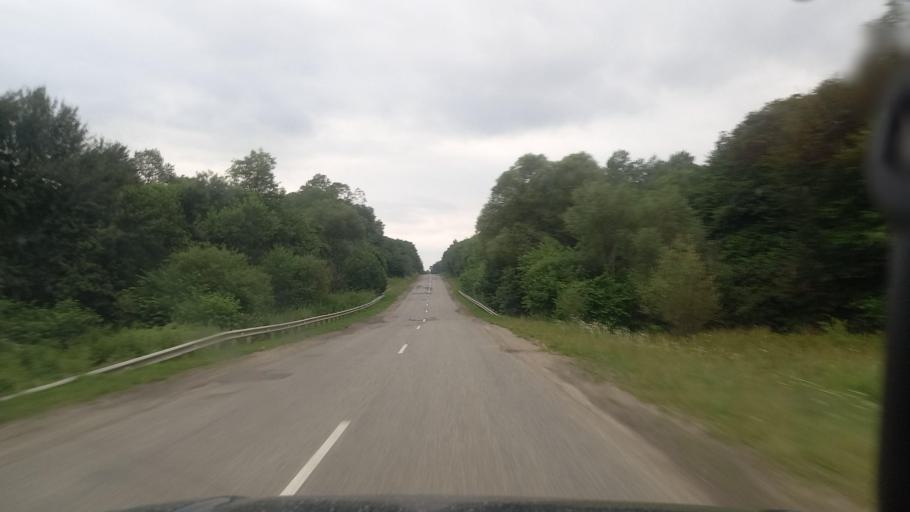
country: RU
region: Karachayevo-Cherkesiya
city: Mednogorskiy
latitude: 43.9421
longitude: 41.1356
